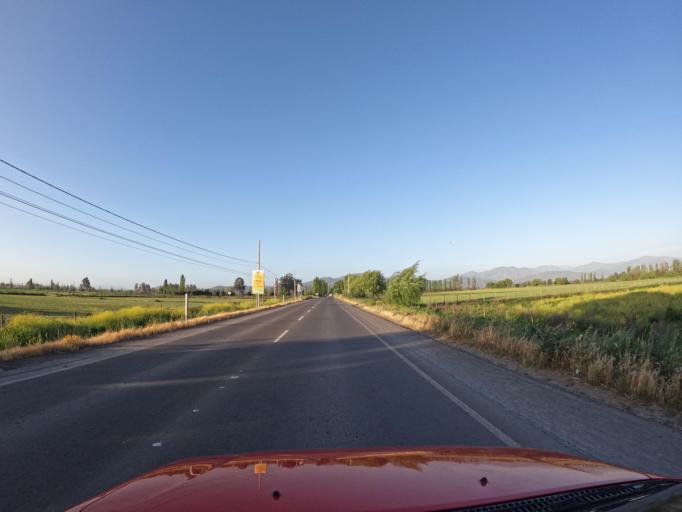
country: CL
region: O'Higgins
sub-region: Provincia de Cachapoal
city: San Vicente
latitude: -34.3079
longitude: -71.3813
